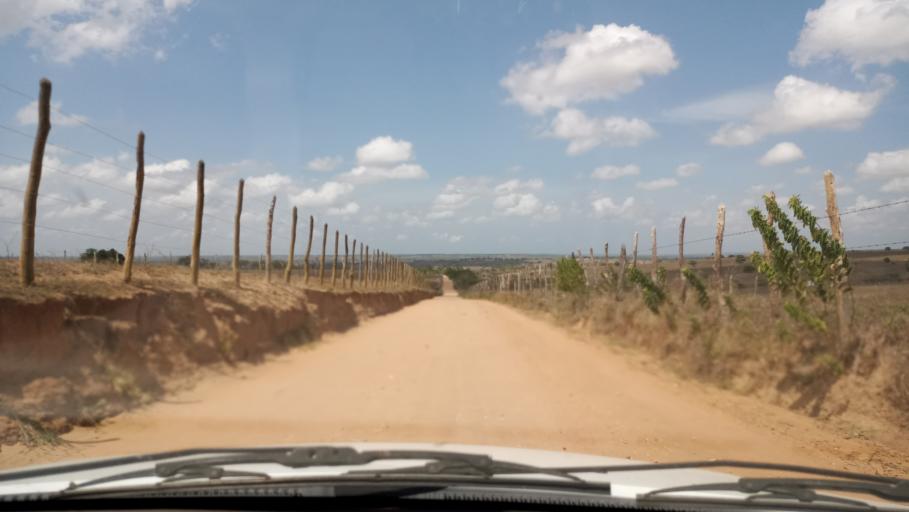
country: BR
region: Rio Grande do Norte
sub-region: Pedro Velho
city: Pedro Velho
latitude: -6.3470
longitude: -35.3302
